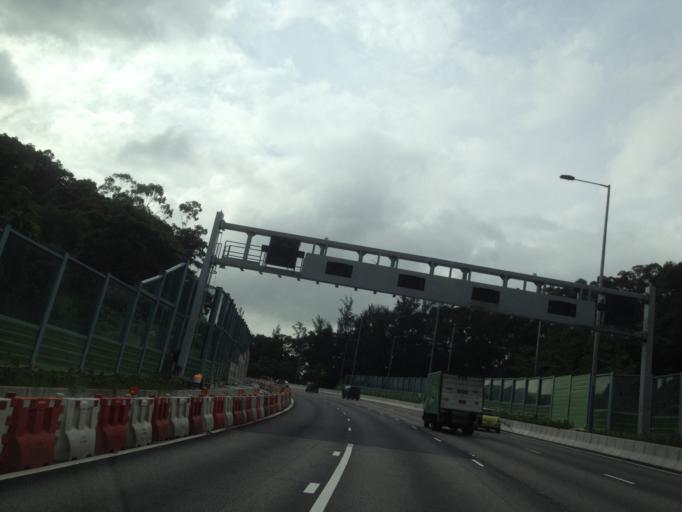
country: HK
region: Tai Po
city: Tai Po
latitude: 22.4433
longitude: 114.1584
